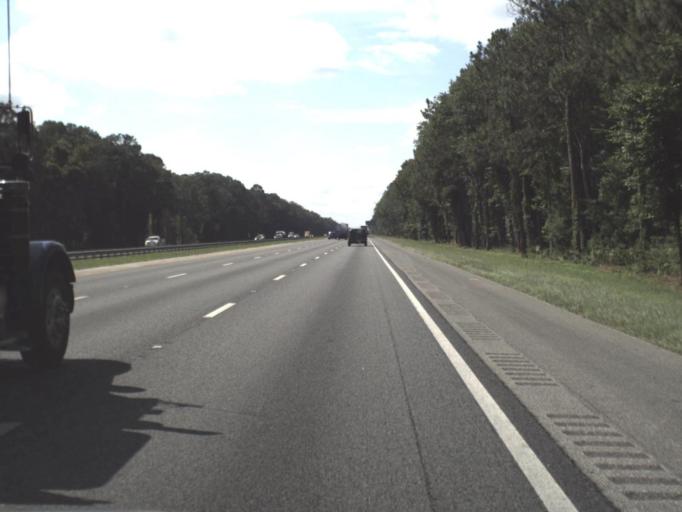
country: US
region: Florida
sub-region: Saint Johns County
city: Villano Beach
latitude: 30.0100
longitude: -81.4764
